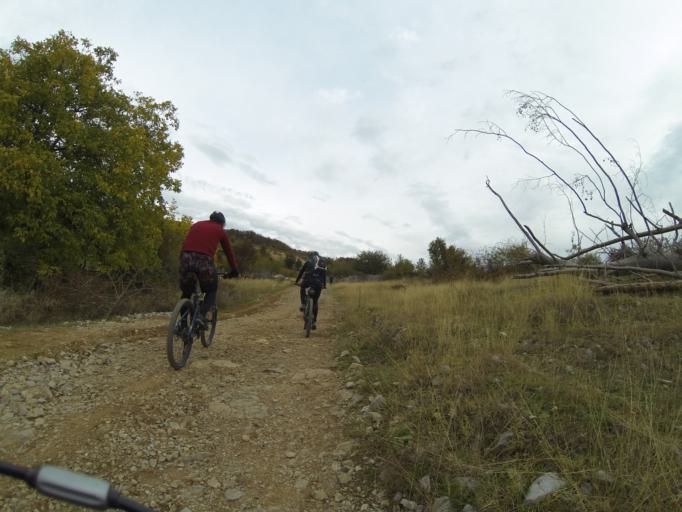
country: RO
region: Gorj
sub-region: Comuna Tismana
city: Sohodol
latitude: 45.0664
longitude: 22.8677
